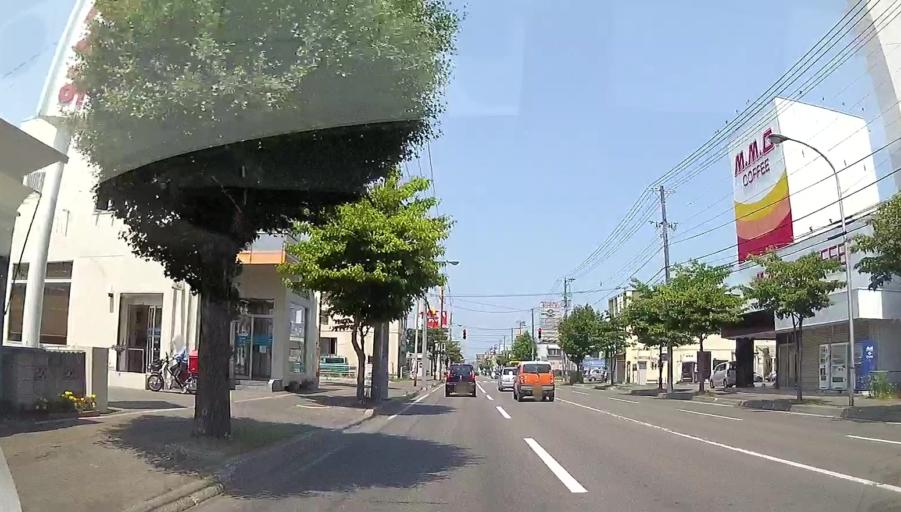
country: JP
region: Hokkaido
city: Obihiro
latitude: 42.9101
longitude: 143.1989
